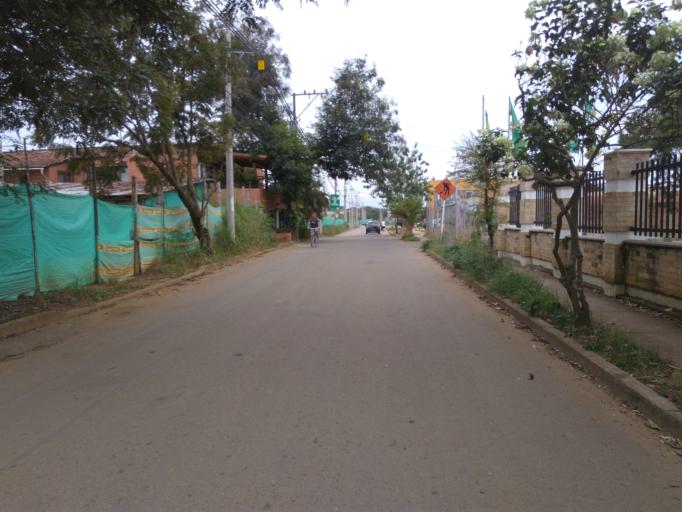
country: CO
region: Valle del Cauca
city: Jamundi
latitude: 3.2578
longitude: -76.5561
